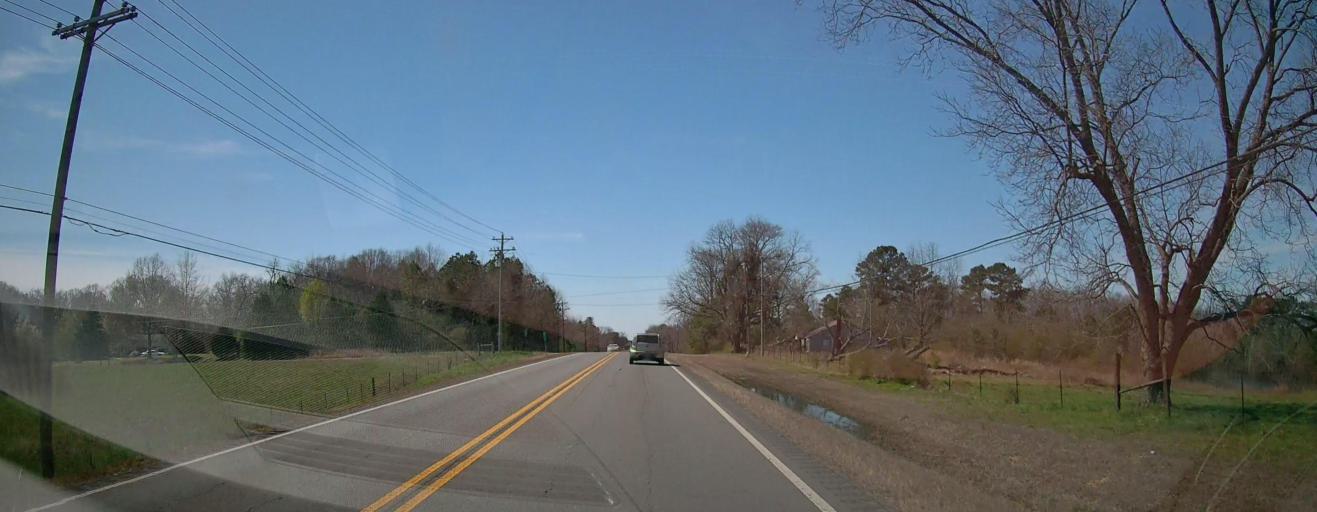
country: US
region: Alabama
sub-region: Blount County
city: Blountsville
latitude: 34.1748
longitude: -86.6433
